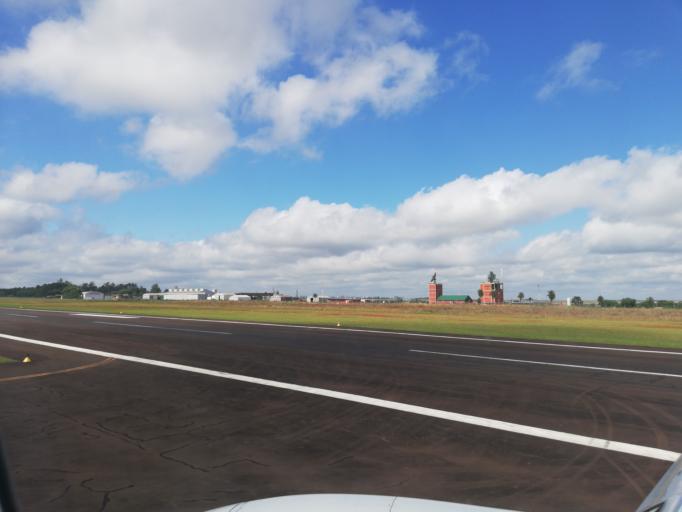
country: AR
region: Misiones
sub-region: Departamento de Capital
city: Posadas
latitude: -27.3896
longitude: -55.9698
